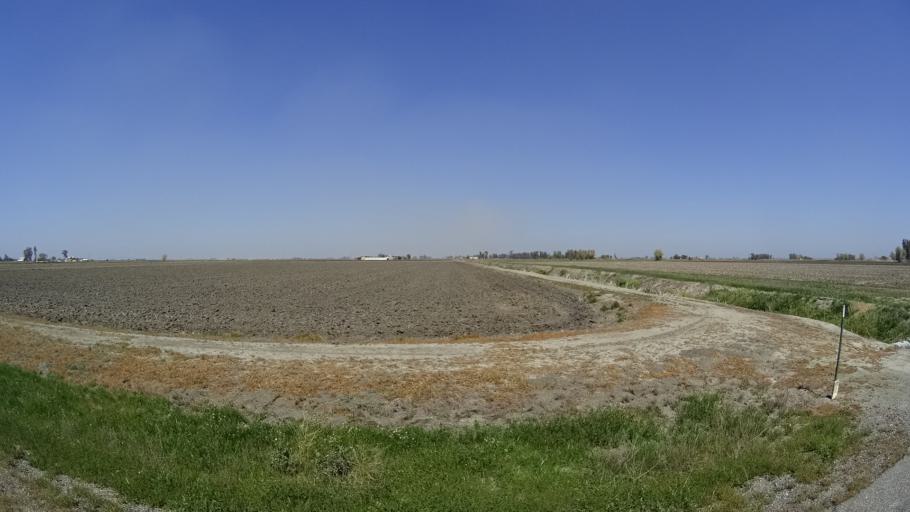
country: US
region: California
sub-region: Glenn County
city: Willows
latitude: 39.5311
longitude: -122.1044
